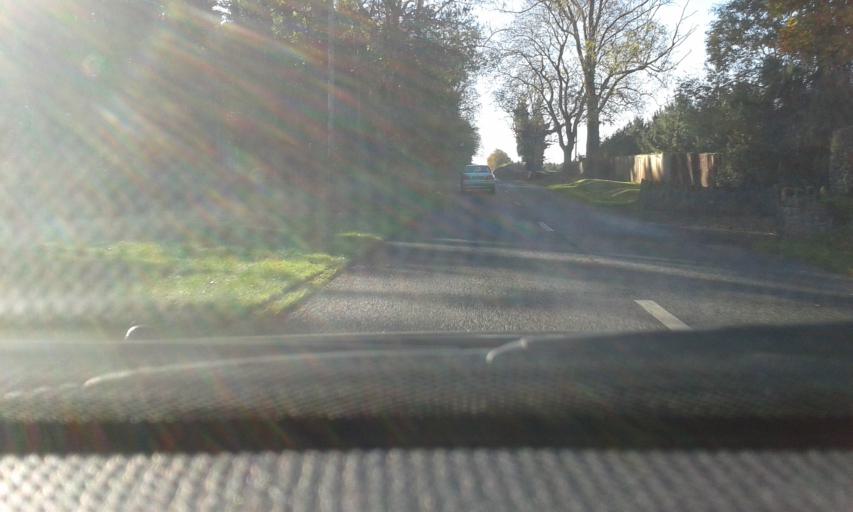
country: IE
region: Leinster
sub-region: Kildare
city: Rathangan
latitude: 53.1905
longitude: -7.0117
